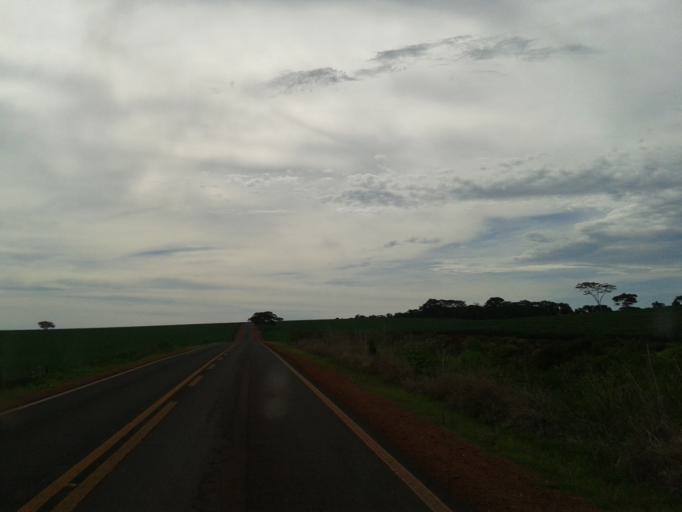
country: BR
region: Minas Gerais
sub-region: Capinopolis
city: Capinopolis
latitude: -18.6915
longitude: -49.4668
